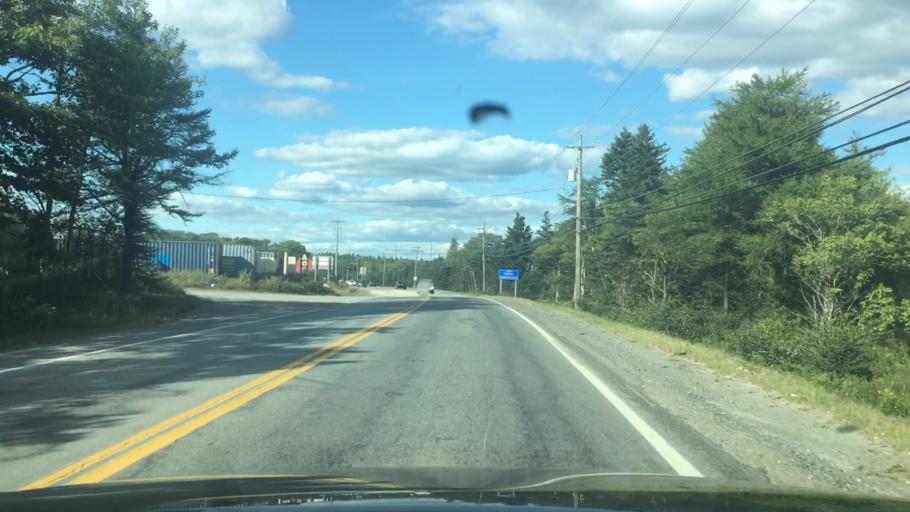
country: CA
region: Nova Scotia
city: Halifax
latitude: 44.6041
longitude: -63.6733
